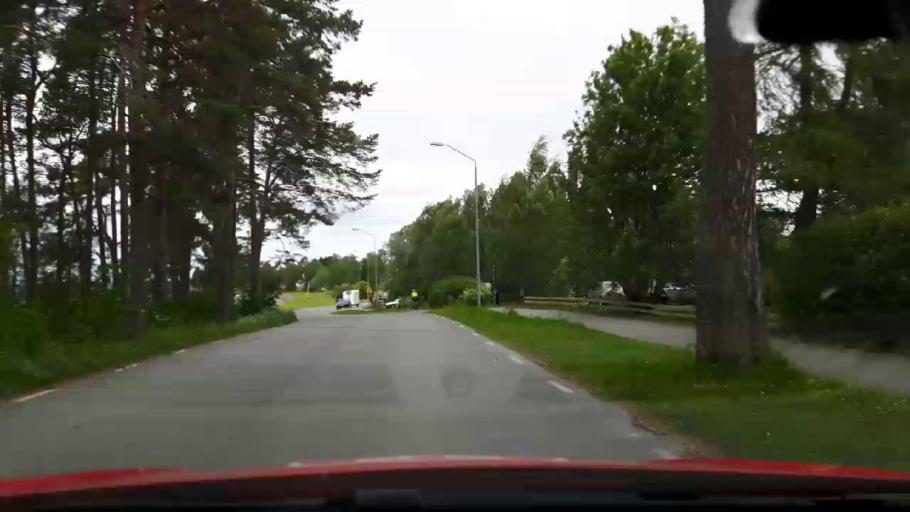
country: SE
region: Jaemtland
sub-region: OEstersunds Kommun
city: Ostersund
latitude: 63.1997
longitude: 14.6380
